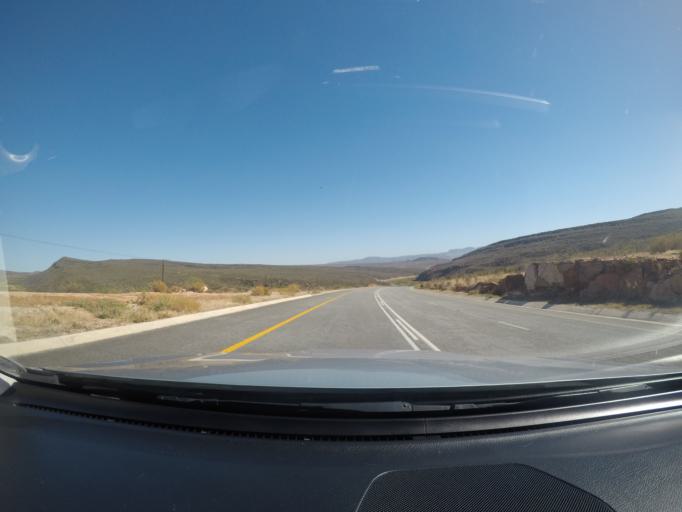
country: ZA
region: Western Cape
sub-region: West Coast District Municipality
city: Clanwilliam
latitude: -32.2308
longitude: 18.8498
